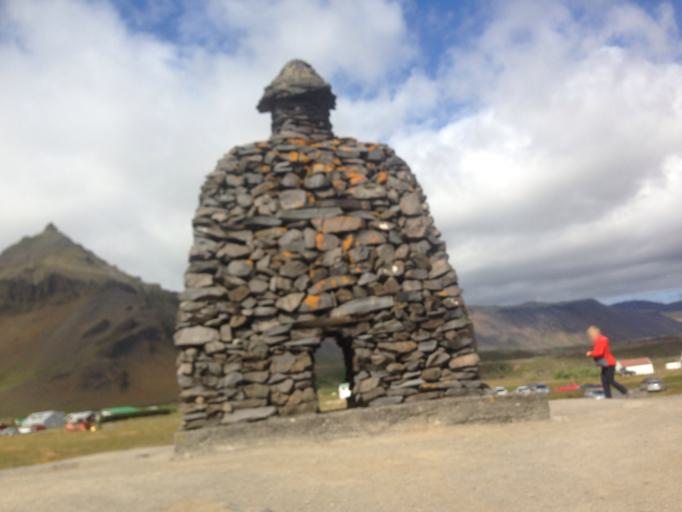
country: IS
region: West
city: Olafsvik
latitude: 64.7656
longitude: -23.6270
